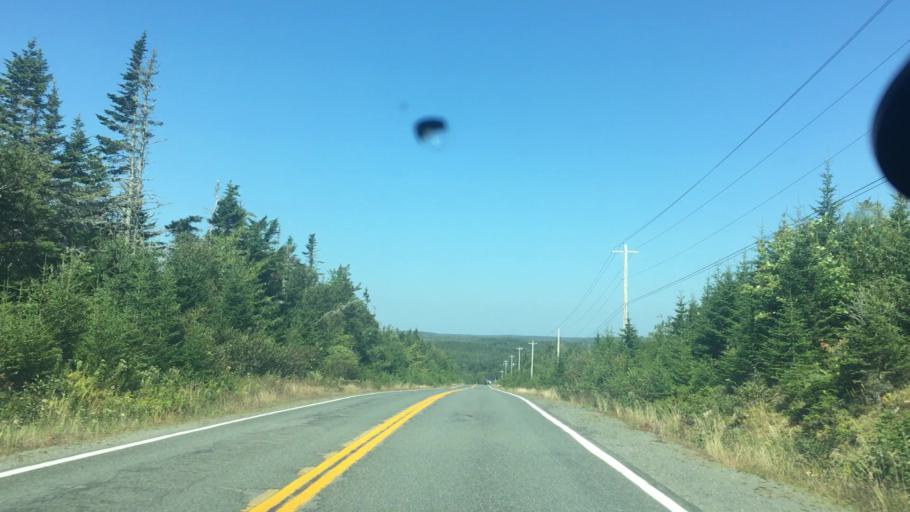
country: CA
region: Nova Scotia
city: Antigonish
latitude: 44.9919
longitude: -62.0967
